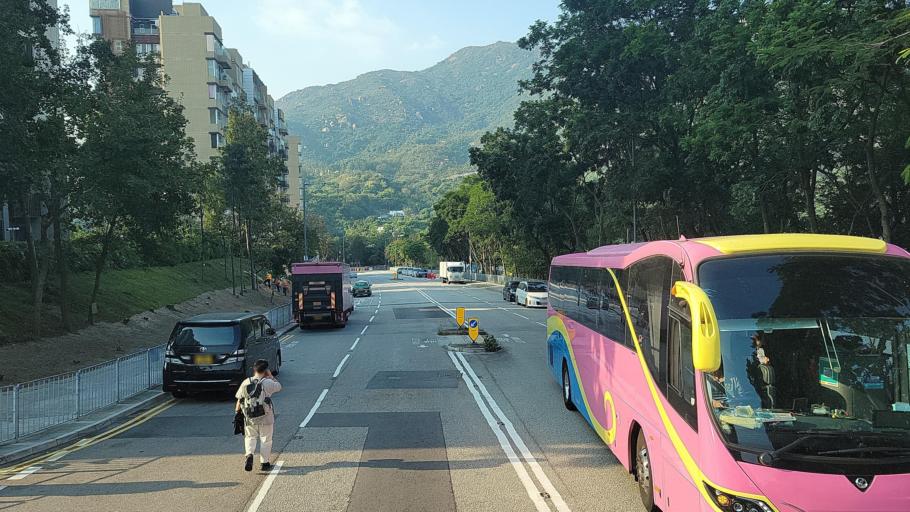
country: HK
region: Tuen Mun
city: Tuen Mun
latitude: 22.3739
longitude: 114.0027
